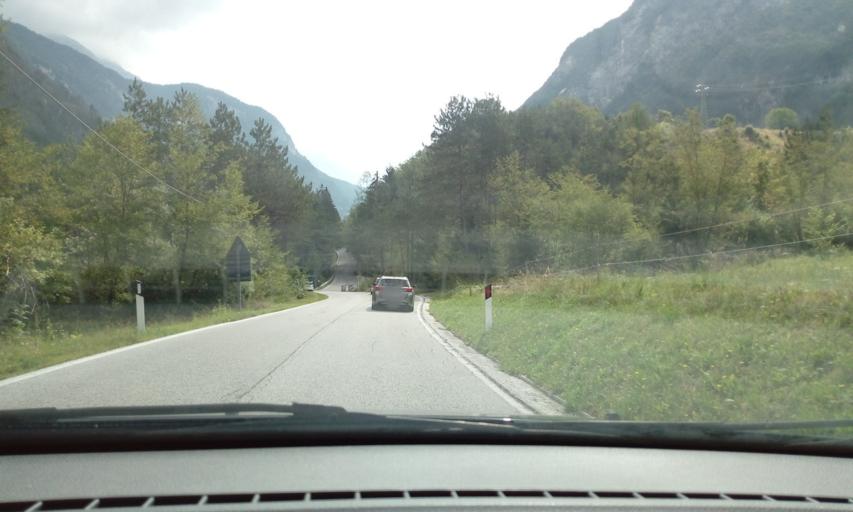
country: IT
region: Friuli Venezia Giulia
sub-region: Provincia di Udine
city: Chiusaforte
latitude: 46.4017
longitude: 13.3975
